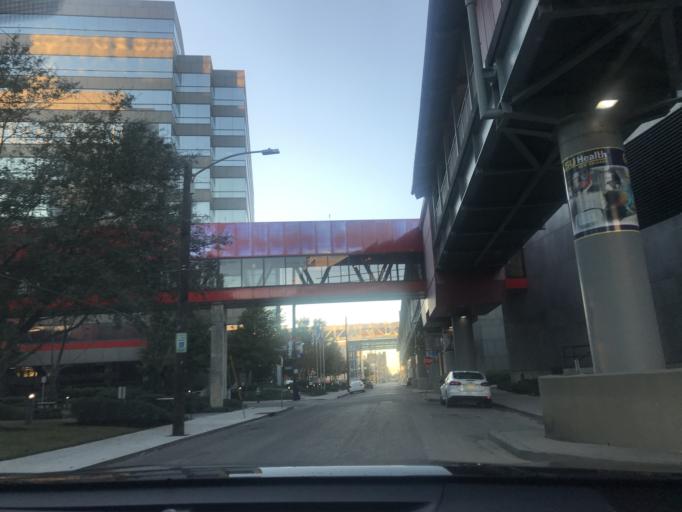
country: US
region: Louisiana
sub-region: Orleans Parish
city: New Orleans
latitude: 29.9566
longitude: -90.0827
